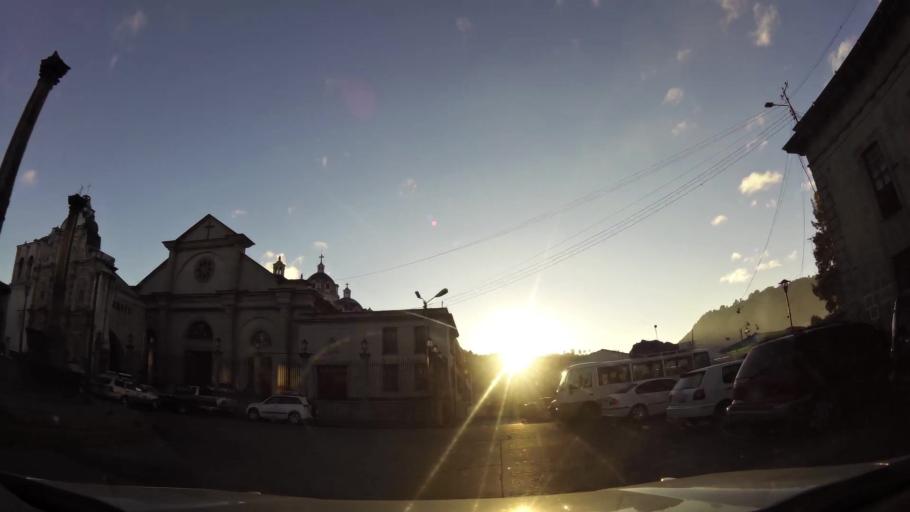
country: GT
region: Quetzaltenango
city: Quetzaltenango
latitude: 14.8335
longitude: -91.5185
